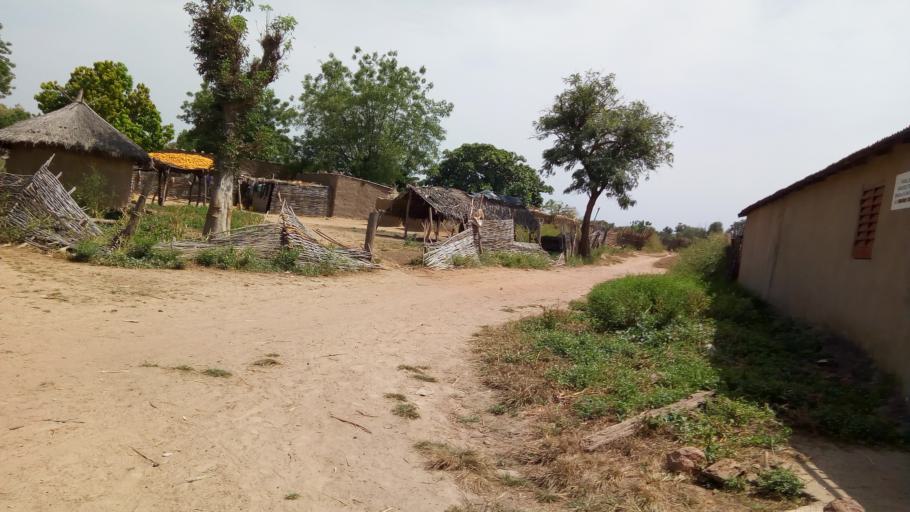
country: ML
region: Kayes
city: Kita
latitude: 13.3996
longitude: -8.8588
